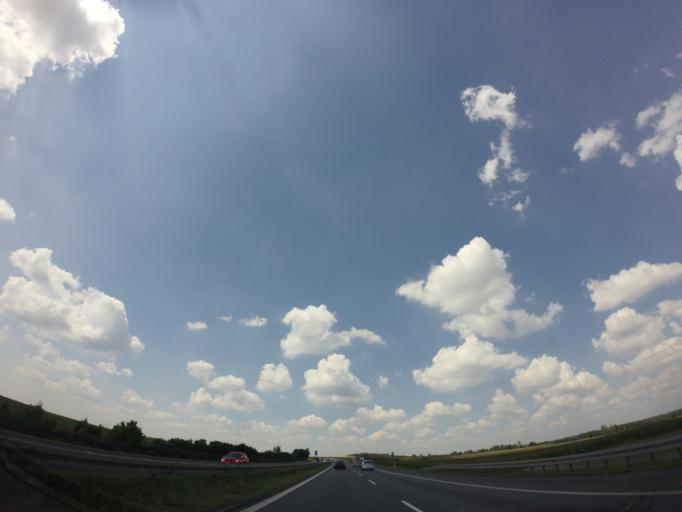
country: PL
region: Opole Voivodeship
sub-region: Powiat opolski
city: Proszkow
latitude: 50.5752
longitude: 17.8485
